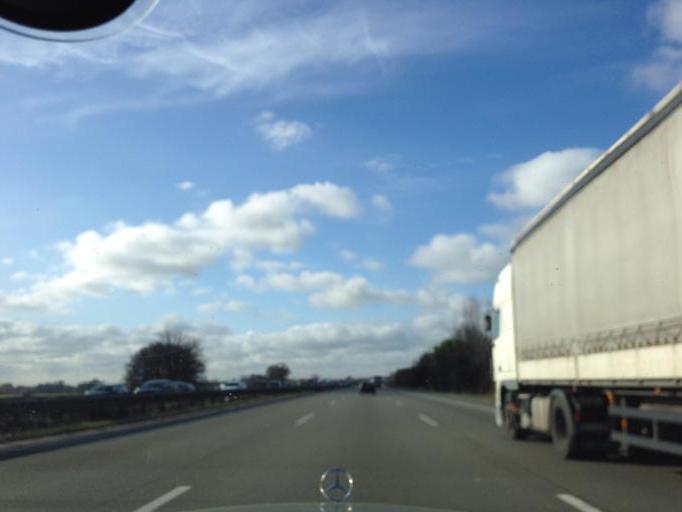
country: DE
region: Hamburg
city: Harburg
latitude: 53.4350
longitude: 10.0323
